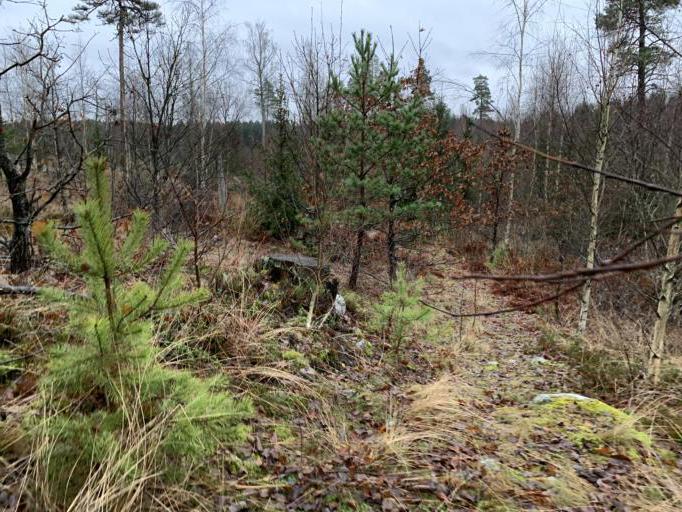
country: SE
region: Soedermanland
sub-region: Eskilstuna Kommun
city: Kvicksund
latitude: 59.3677
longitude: 16.2869
